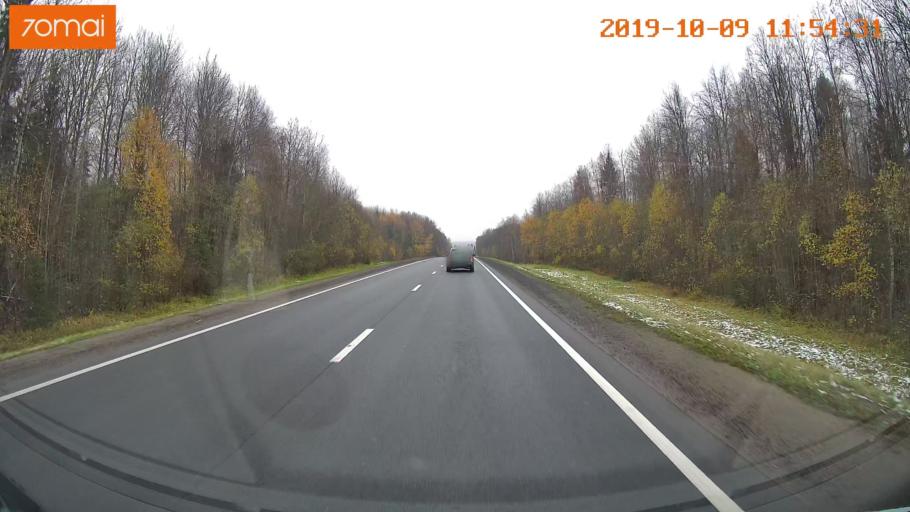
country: RU
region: Vologda
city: Gryazovets
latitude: 58.7583
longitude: 40.2817
